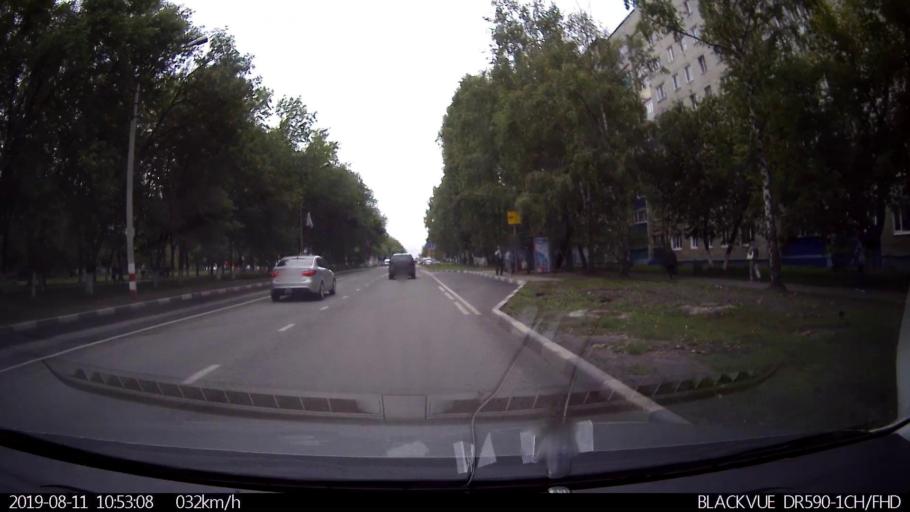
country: RU
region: Ulyanovsk
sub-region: Ulyanovskiy Rayon
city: Ulyanovsk
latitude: 54.2613
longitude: 48.3343
